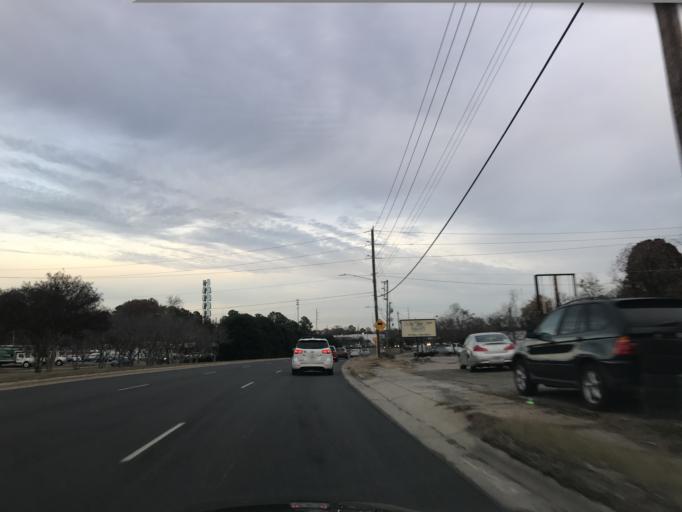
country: US
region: North Carolina
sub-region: Wake County
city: Raleigh
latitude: 35.7978
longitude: -78.6393
